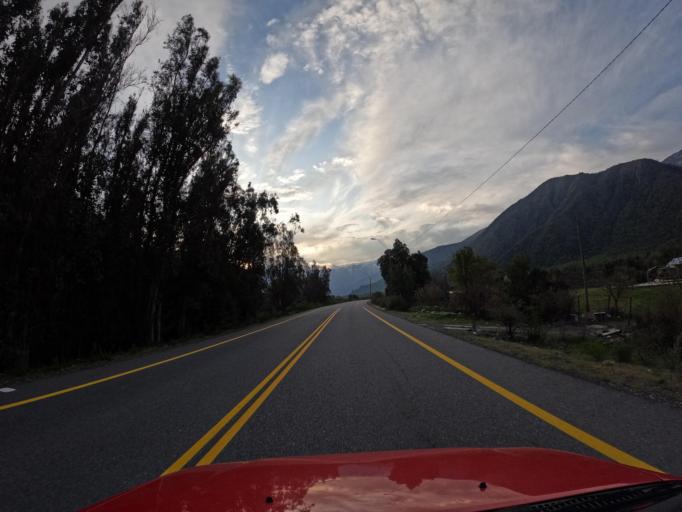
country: CL
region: Maule
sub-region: Provincia de Linares
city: Colbun
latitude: -35.7259
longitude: -71.0238
